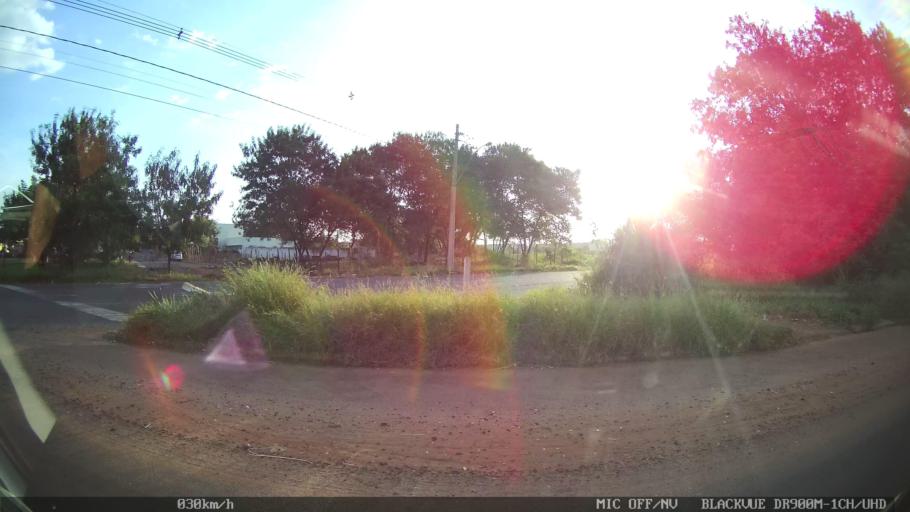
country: BR
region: Sao Paulo
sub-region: Ribeirao Preto
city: Ribeirao Preto
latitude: -21.1184
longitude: -47.8038
